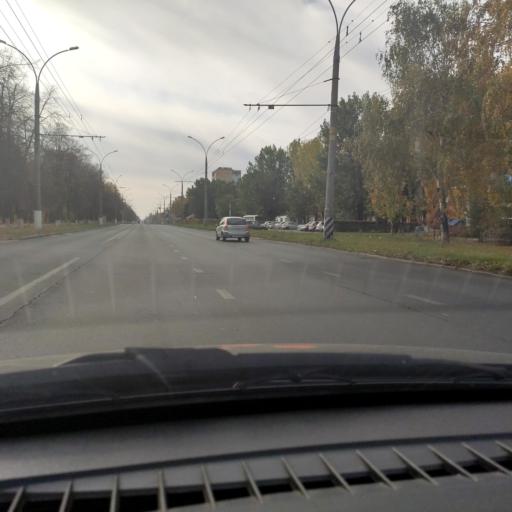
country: RU
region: Samara
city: Tol'yatti
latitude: 53.5357
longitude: 49.2778
